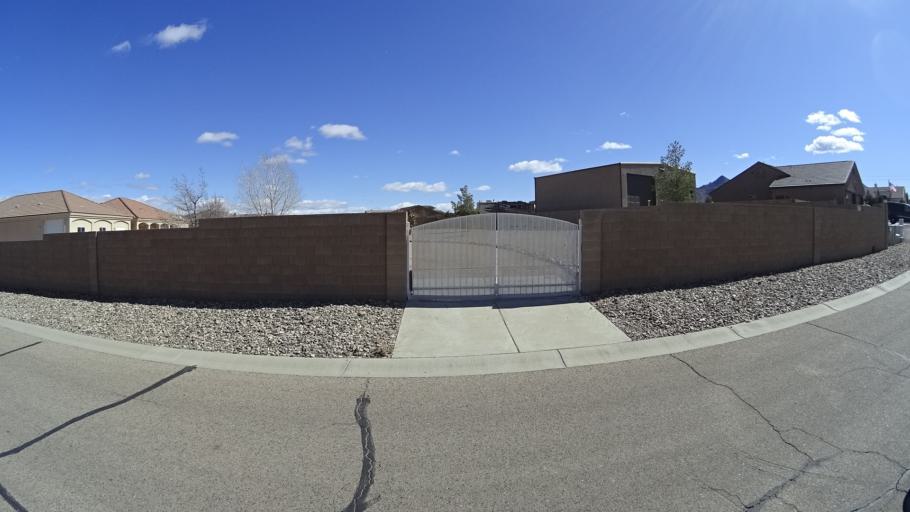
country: US
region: Arizona
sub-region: Mohave County
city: Kingman
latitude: 35.2048
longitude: -113.9698
